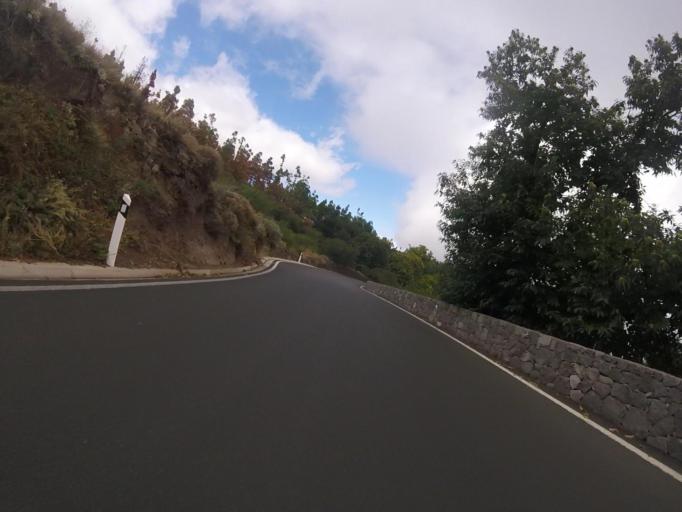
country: ES
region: Canary Islands
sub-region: Provincia de Las Palmas
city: San Bartolome
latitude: 27.9712
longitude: -15.5726
